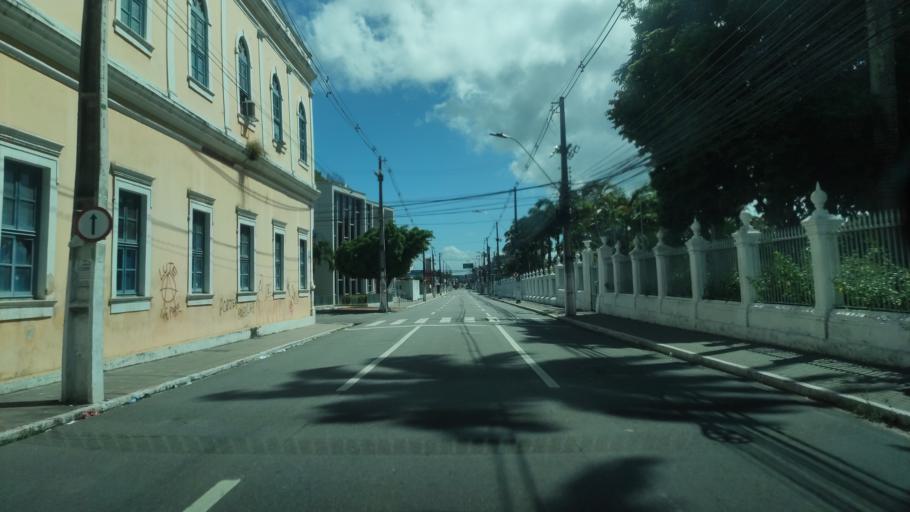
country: BR
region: Alagoas
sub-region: Maceio
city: Maceio
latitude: -9.6606
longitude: -35.7394
